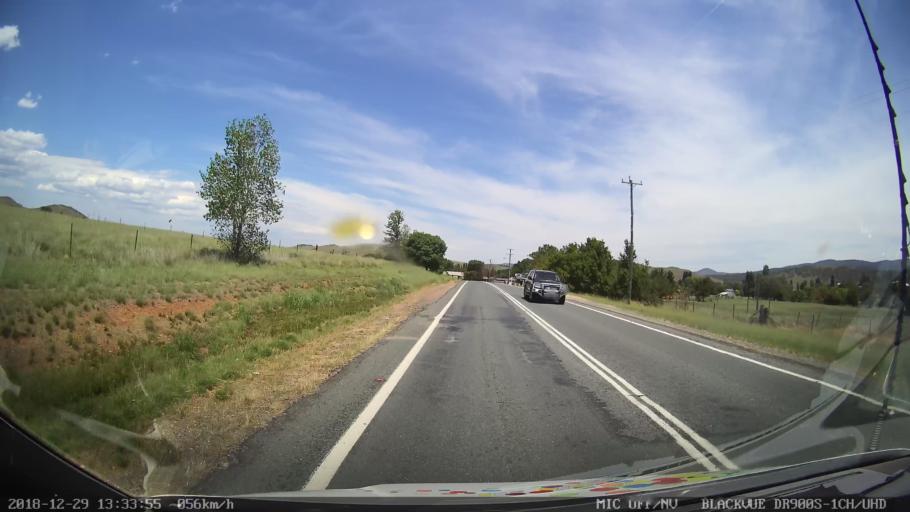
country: AU
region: New South Wales
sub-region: Cooma-Monaro
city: Cooma
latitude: -35.9494
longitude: 149.1458
